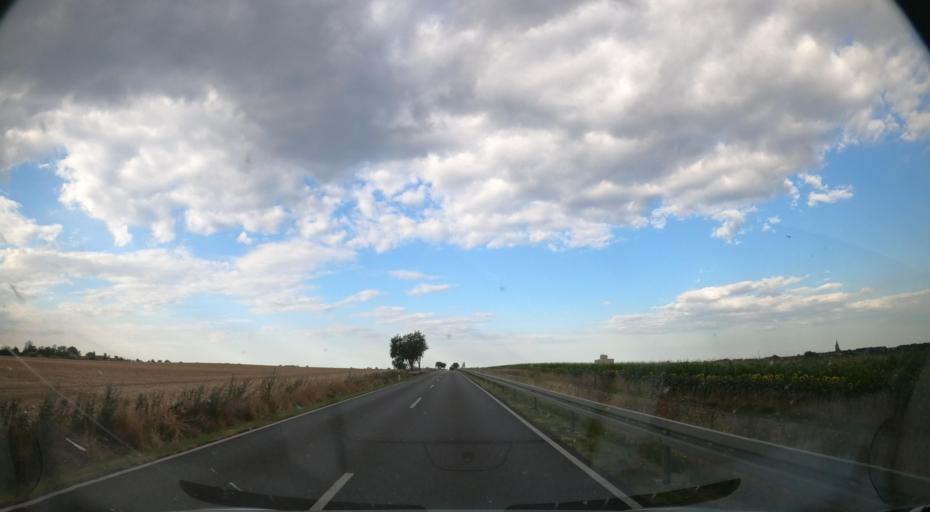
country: DE
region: Mecklenburg-Vorpommern
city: Pasewalk
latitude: 53.5042
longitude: 13.9584
